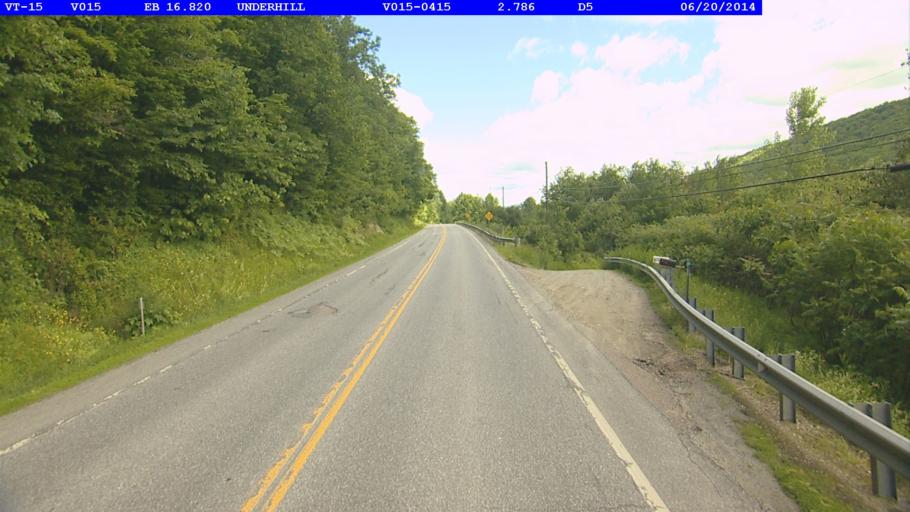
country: US
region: Vermont
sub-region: Chittenden County
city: Jericho
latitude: 44.5639
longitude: -72.9421
